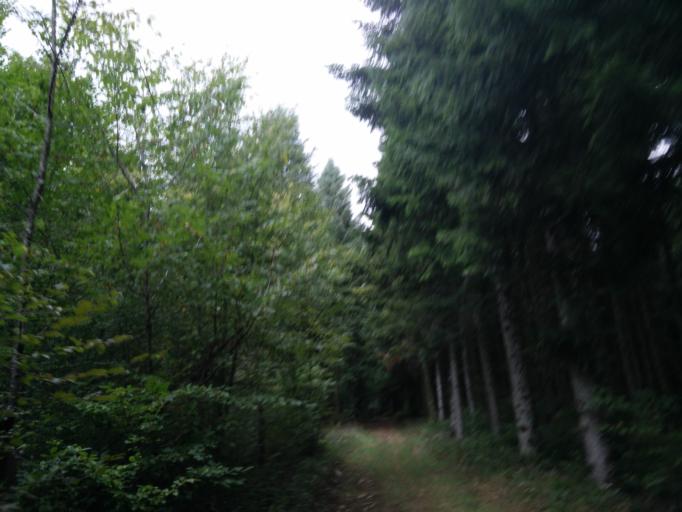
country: FR
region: Franche-Comte
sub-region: Departement du Doubs
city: Mamirolle
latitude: 47.2169
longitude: 6.1440
